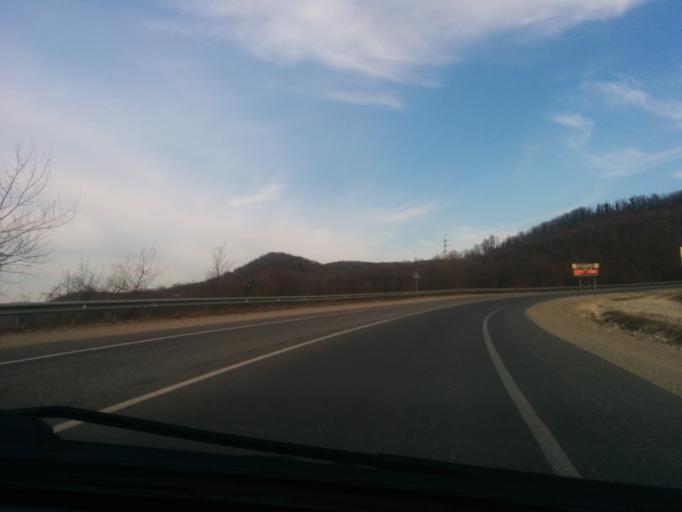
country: RU
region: Krasnodarskiy
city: Novomikhaylovskiy
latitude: 44.2578
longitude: 38.8801
